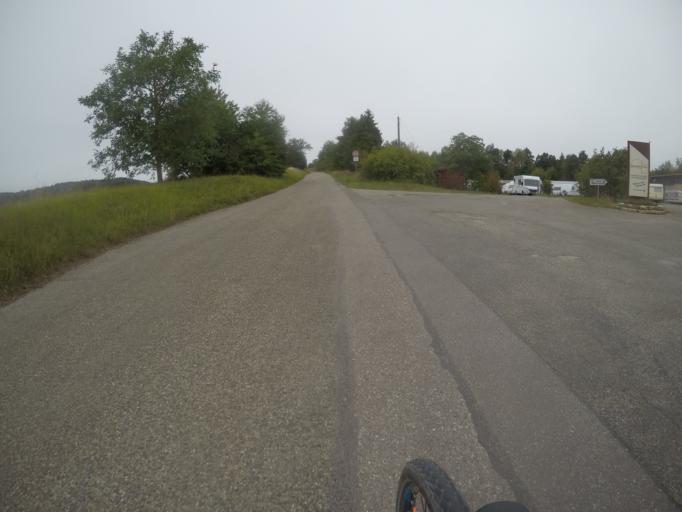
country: DE
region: Baden-Wuerttemberg
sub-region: Karlsruhe Region
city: Simmozheim
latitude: 48.7717
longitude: 8.8376
